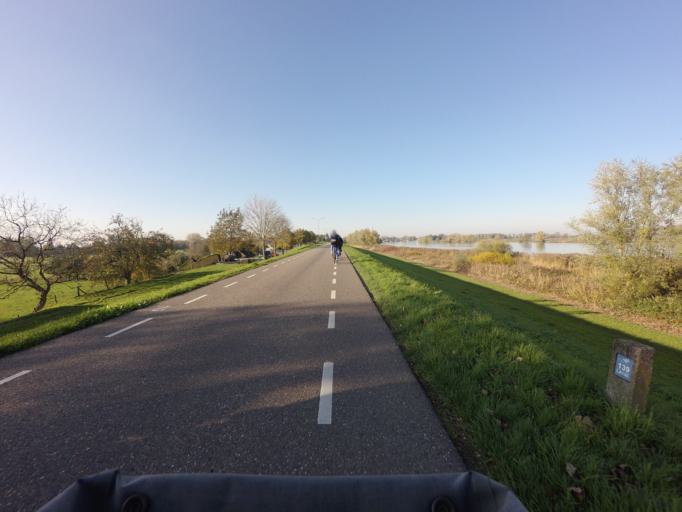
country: NL
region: North Brabant
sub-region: Gemeente Woudrichem
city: Woudrichem
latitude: 51.8043
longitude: 5.0184
